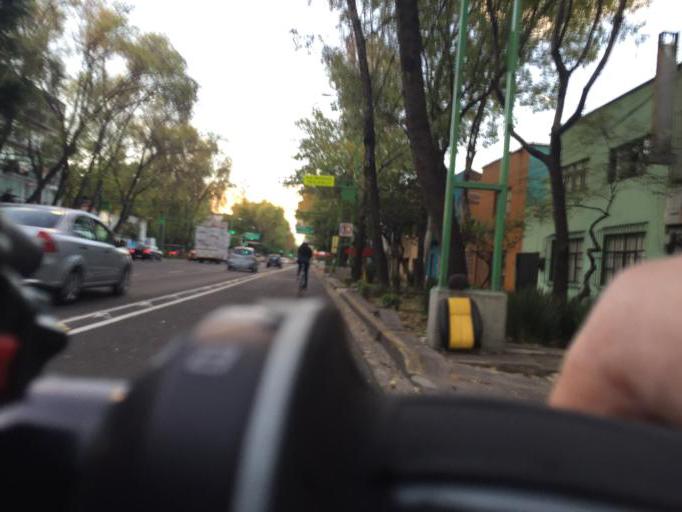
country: MX
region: Mexico City
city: Benito Juarez
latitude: 19.3968
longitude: -99.1458
